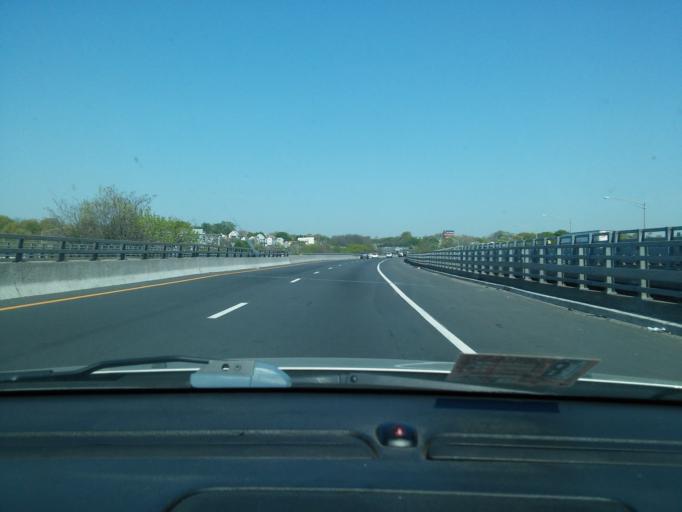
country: US
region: New Jersey
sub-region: Essex County
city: Newark
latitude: 40.7098
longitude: -74.1945
